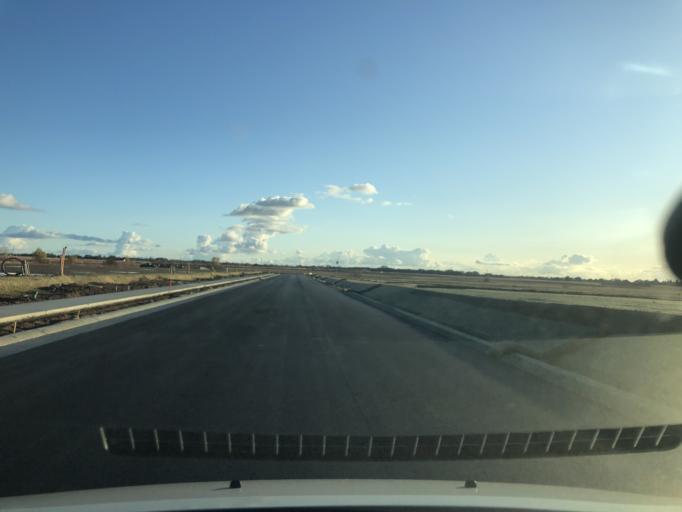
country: US
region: California
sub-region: Sacramento County
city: Antelope
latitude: 38.7581
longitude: -121.3678
